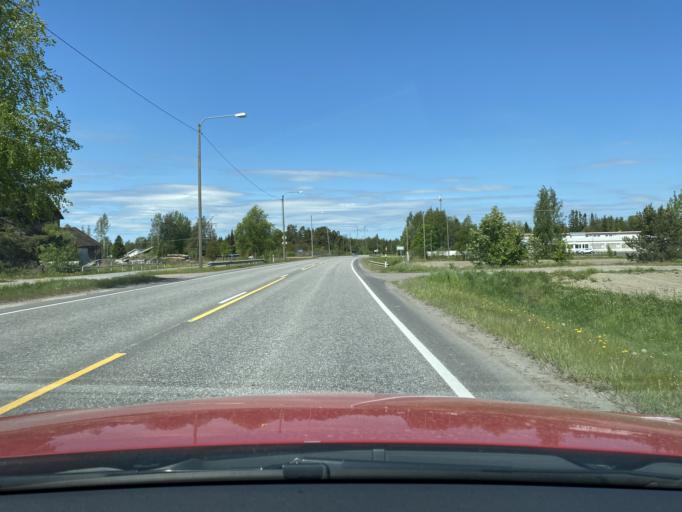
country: FI
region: Satakunta
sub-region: Rauma
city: Eura
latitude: 61.1227
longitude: 22.1324
